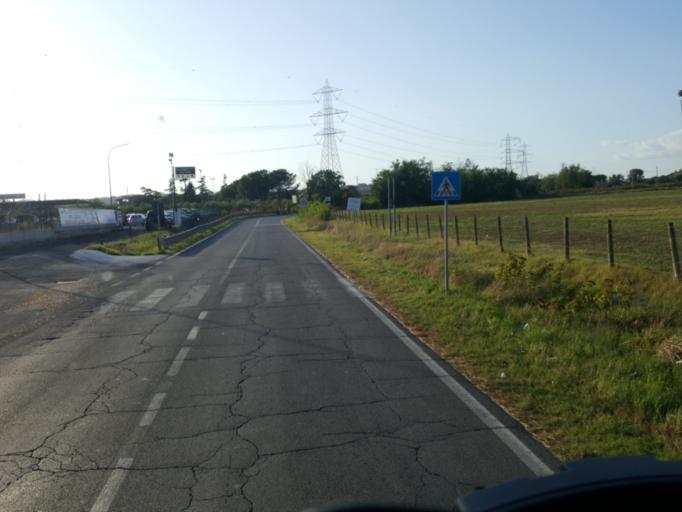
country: IT
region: Latium
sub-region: Citta metropolitana di Roma Capitale
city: Bivio di Capanelle
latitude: 42.1244
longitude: 12.5777
